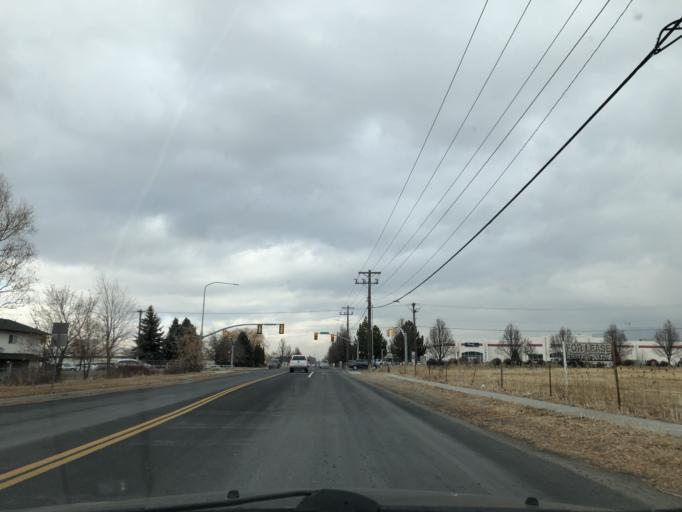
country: US
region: Utah
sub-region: Cache County
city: Logan
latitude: 41.7569
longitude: -111.8392
